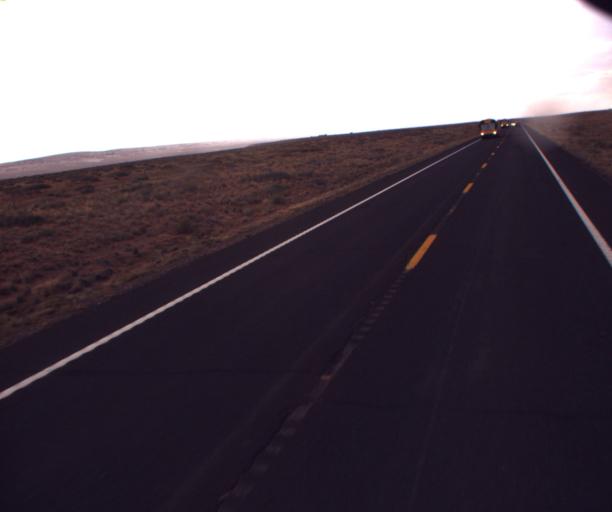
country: US
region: Arizona
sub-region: Coconino County
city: Tuba City
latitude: 36.1727
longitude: -111.0850
